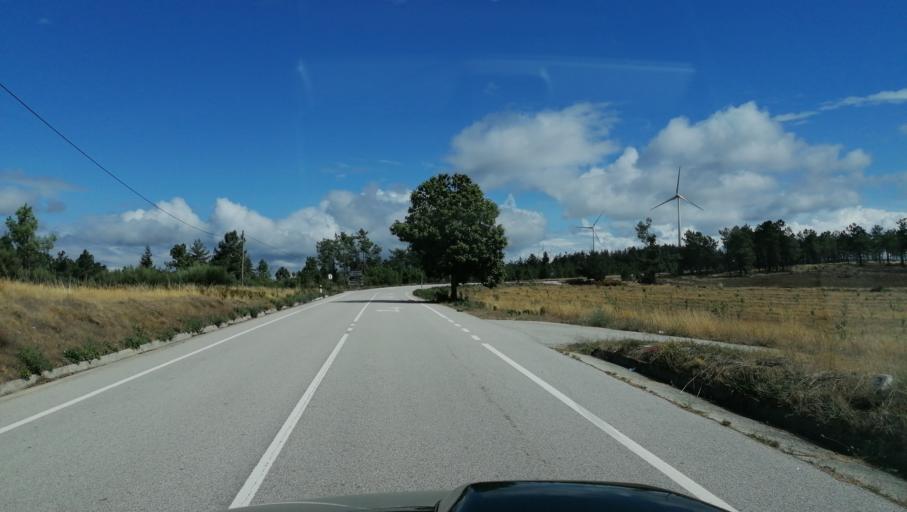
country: PT
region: Vila Real
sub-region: Vila Pouca de Aguiar
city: Vila Pouca de Aguiar
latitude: 41.5239
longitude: -7.5930
